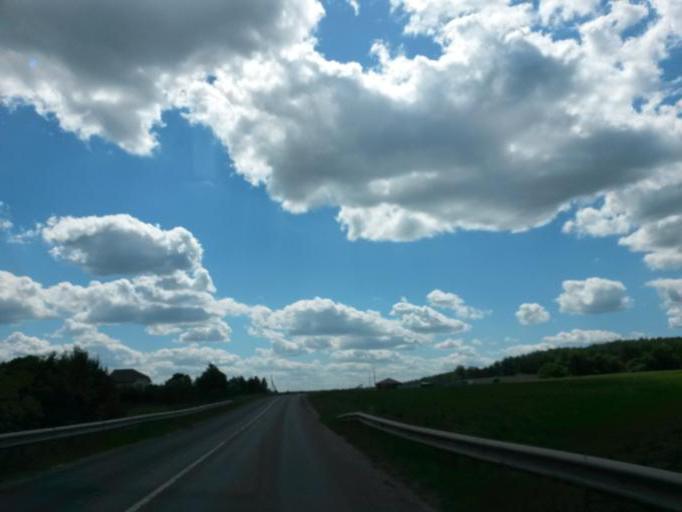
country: RU
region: Moskovskaya
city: Lyubuchany
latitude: 55.2928
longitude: 37.6292
